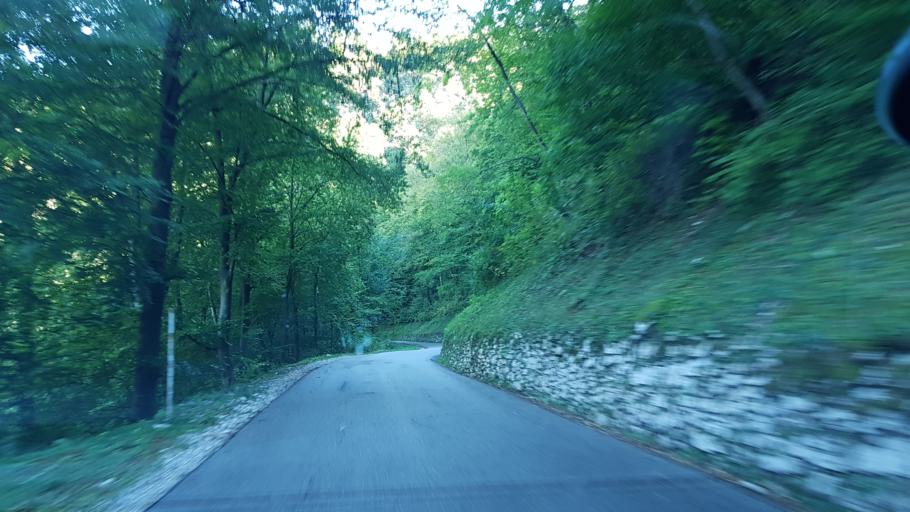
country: SI
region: Kobarid
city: Kobarid
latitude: 46.2562
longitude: 13.5952
